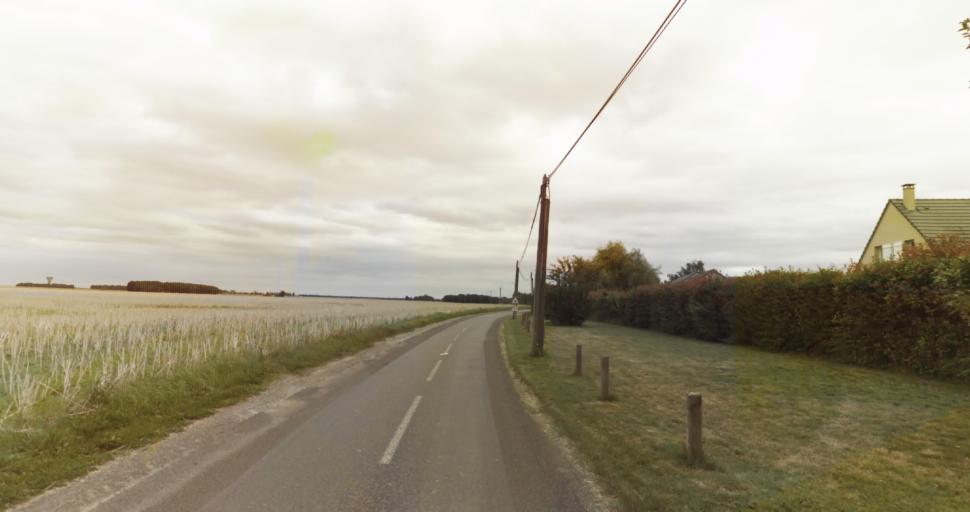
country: FR
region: Haute-Normandie
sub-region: Departement de l'Eure
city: Menilles
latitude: 48.9447
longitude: 1.2668
